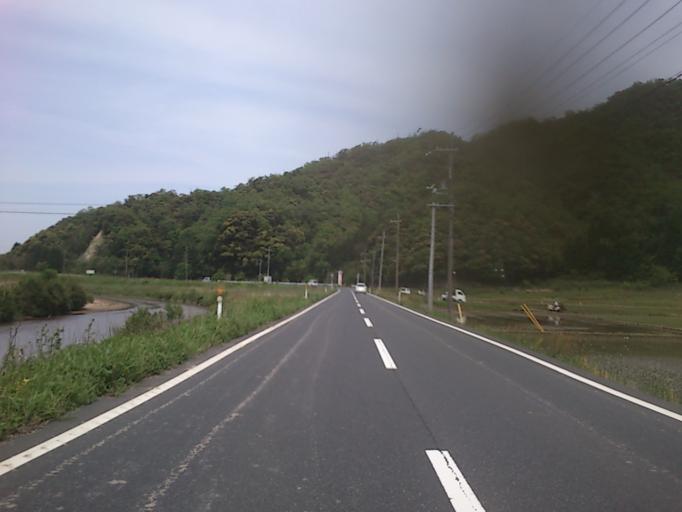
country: JP
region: Kyoto
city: Miyazu
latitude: 35.6957
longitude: 135.1027
